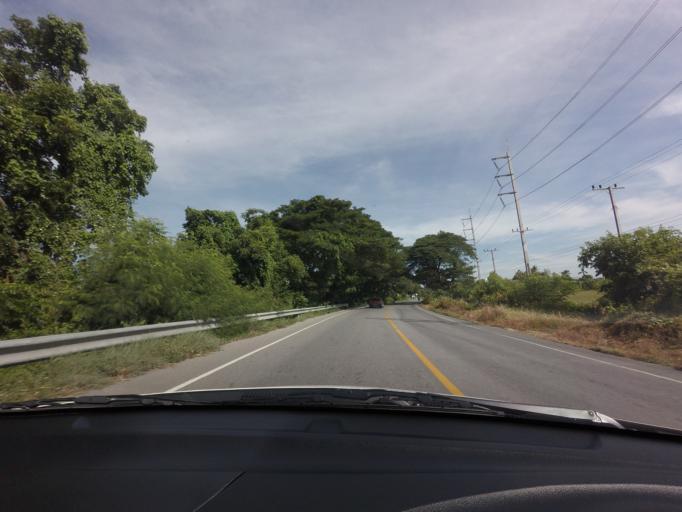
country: TH
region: Suphan Buri
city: Don Chedi
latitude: 14.5117
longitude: 99.9645
